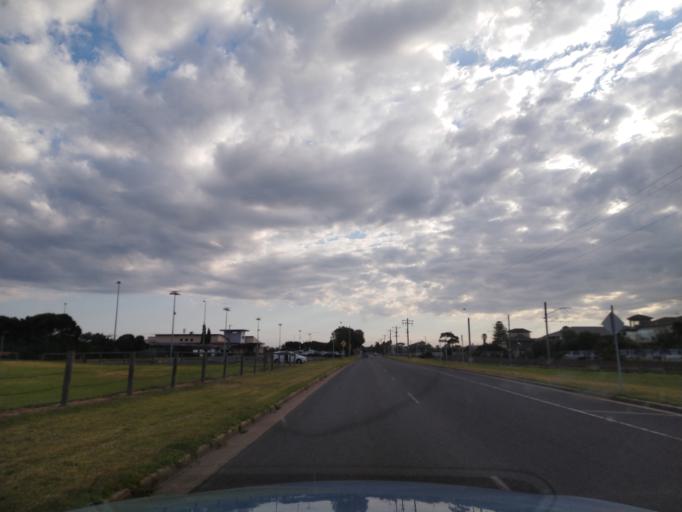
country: AU
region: Victoria
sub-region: Hobsons Bay
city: Seaholme
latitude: -37.8628
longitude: 144.8493
